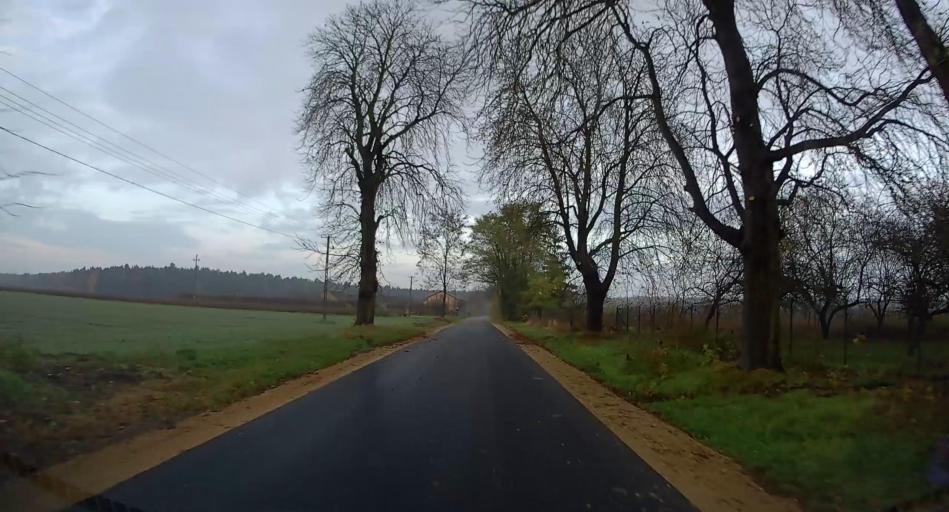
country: PL
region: Lodz Voivodeship
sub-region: Powiat skierniewicki
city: Kowiesy
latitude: 51.9267
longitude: 20.4044
